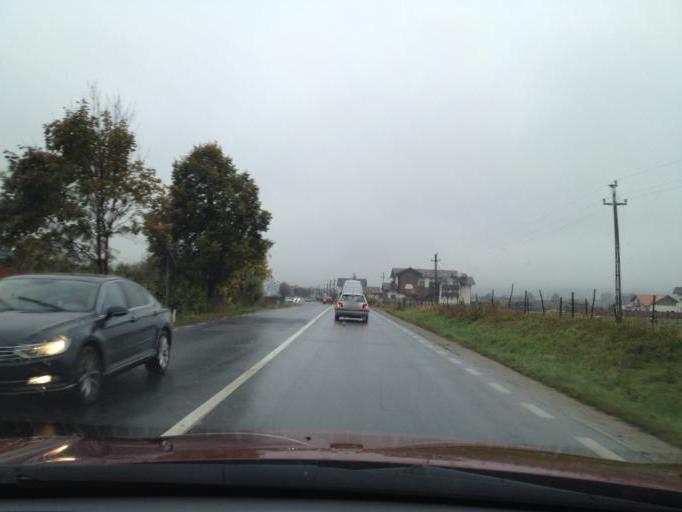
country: RO
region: Brasov
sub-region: Comuna Zarnesti
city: Tohanu Nou
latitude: 45.5376
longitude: 25.3772
